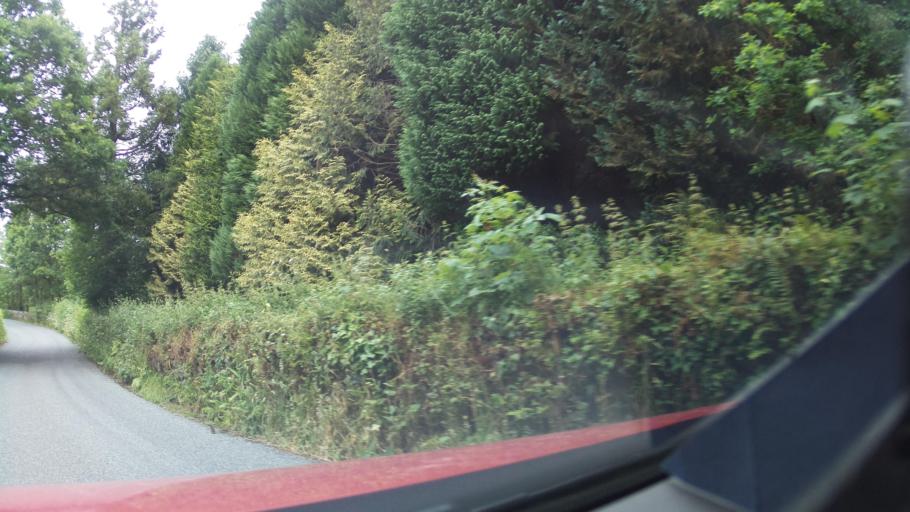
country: GB
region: England
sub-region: Devon
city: Bovey Tracey
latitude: 50.6726
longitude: -3.6527
